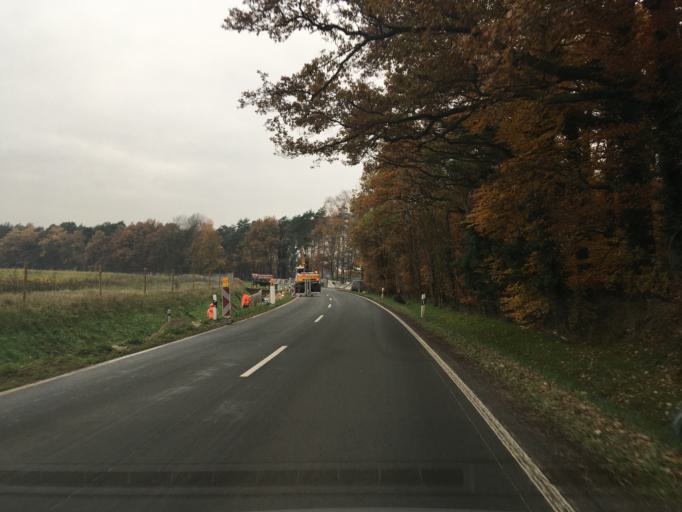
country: DE
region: North Rhine-Westphalia
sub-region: Regierungsbezirk Munster
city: Legden
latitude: 52.0290
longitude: 7.0716
